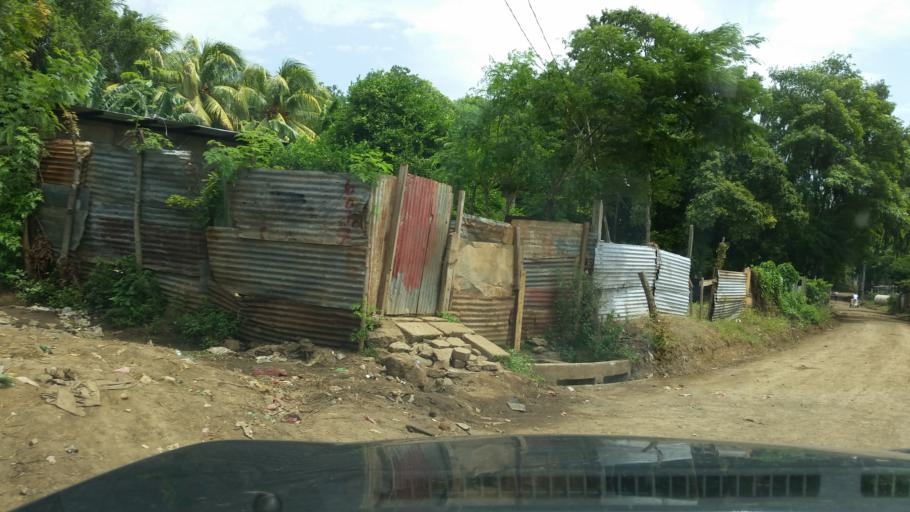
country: NI
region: Managua
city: Managua
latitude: 12.1146
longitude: -86.2213
